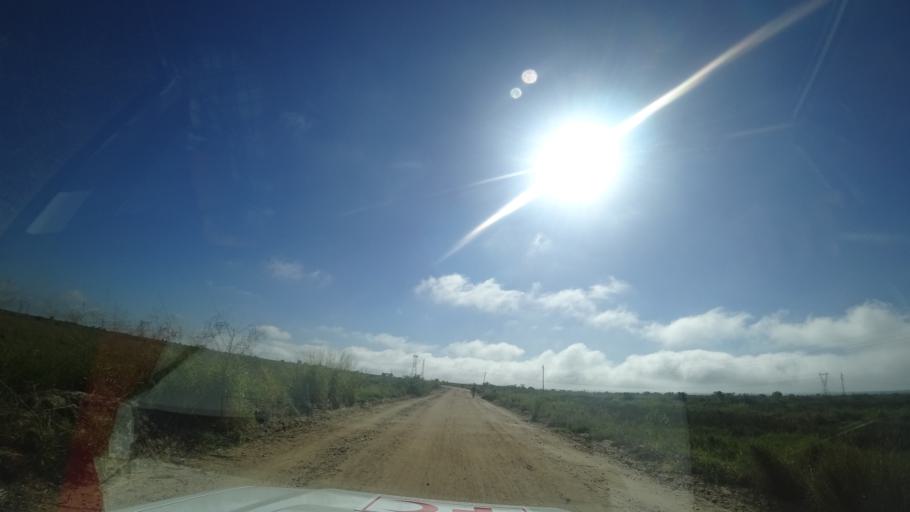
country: MZ
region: Sofala
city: Dondo
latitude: -19.4632
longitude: 34.5619
